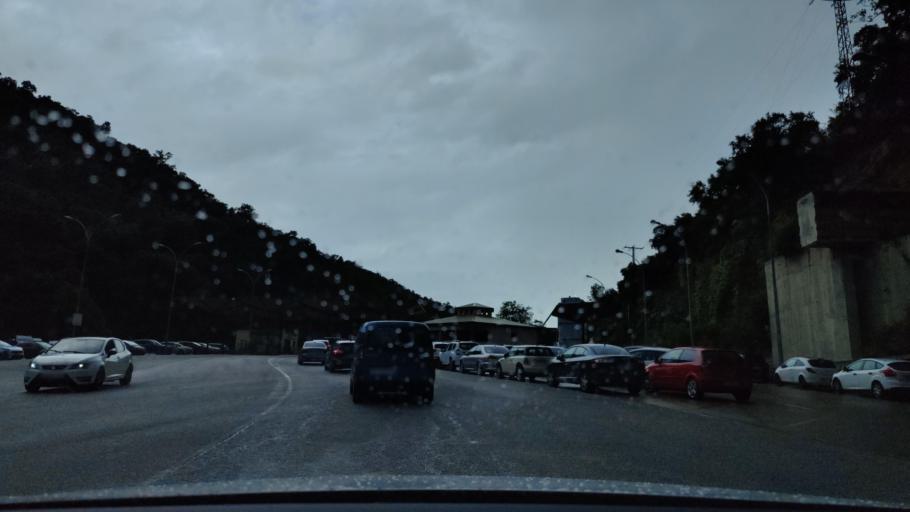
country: ES
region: Catalonia
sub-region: Provincia de Girona
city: la Jonquera
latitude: 42.4583
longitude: 2.8645
